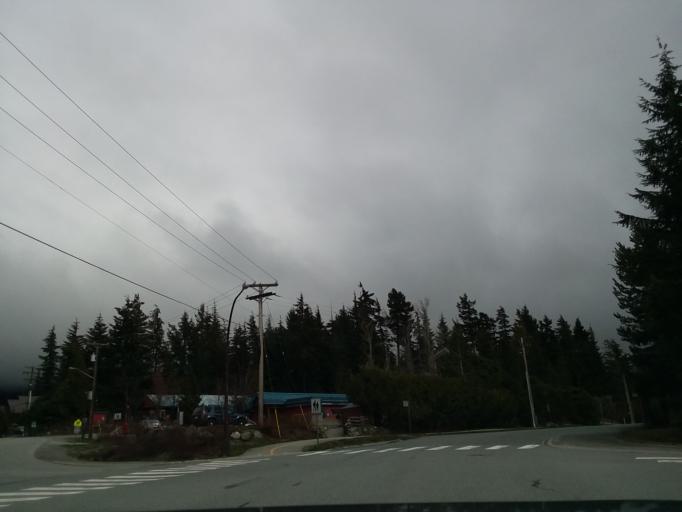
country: CA
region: British Columbia
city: Whistler
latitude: 50.1245
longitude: -122.9618
